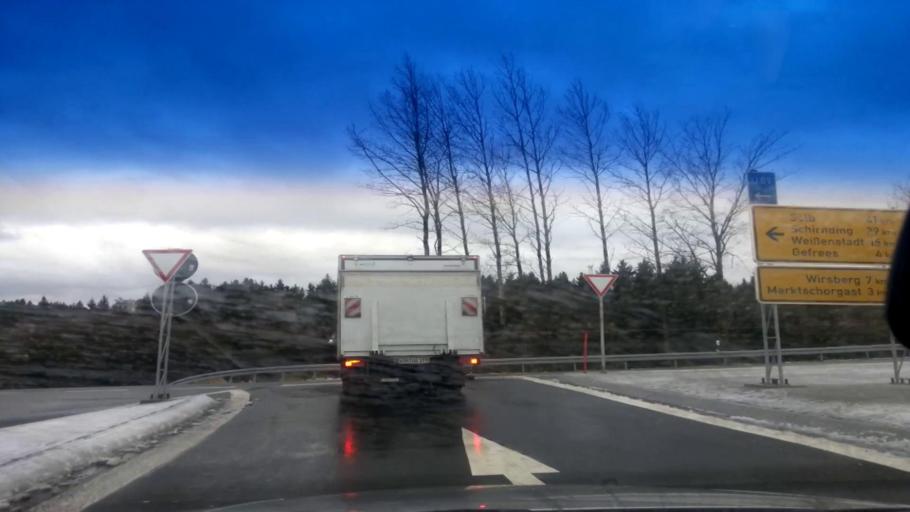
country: DE
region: Bavaria
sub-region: Upper Franconia
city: Gefrees
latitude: 50.0959
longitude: 11.6967
